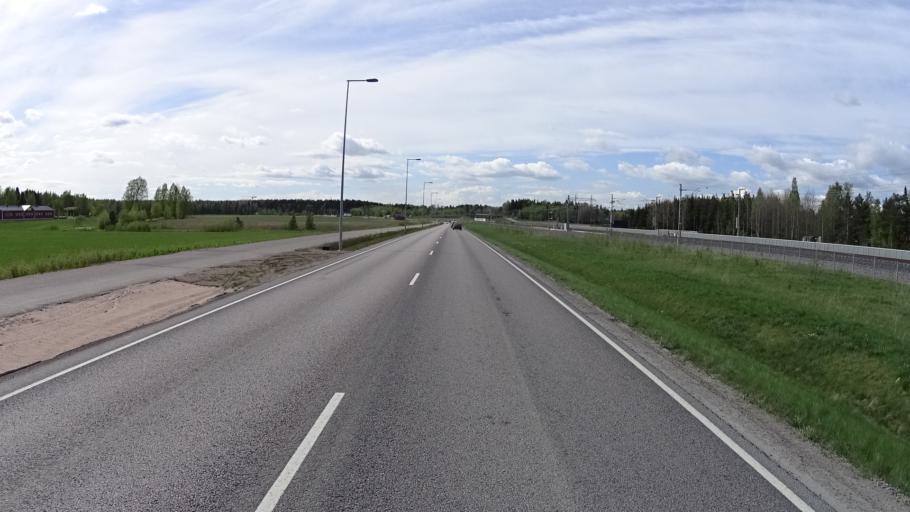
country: FI
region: Uusimaa
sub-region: Helsinki
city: Teekkarikylae
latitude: 60.3144
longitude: 24.8812
